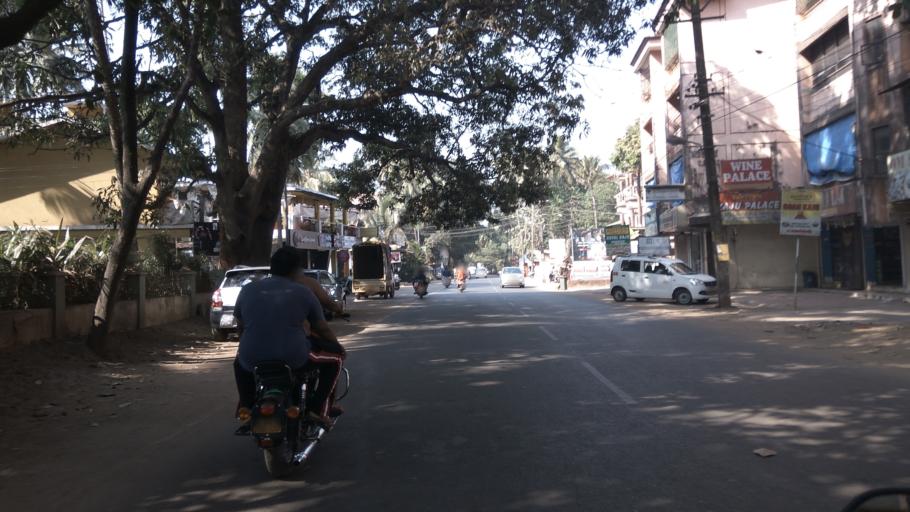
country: IN
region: Goa
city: Calangute
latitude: 15.5489
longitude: 73.7646
